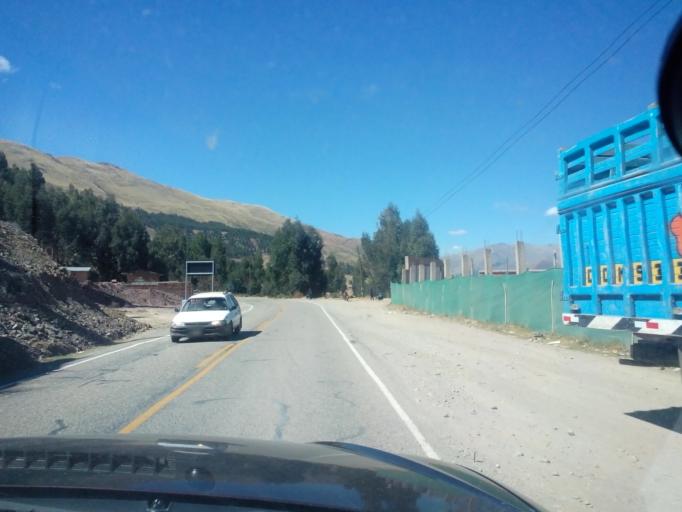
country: PE
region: Cusco
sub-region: Provincia de Canchis
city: Combapata
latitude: -14.1027
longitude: -71.4266
